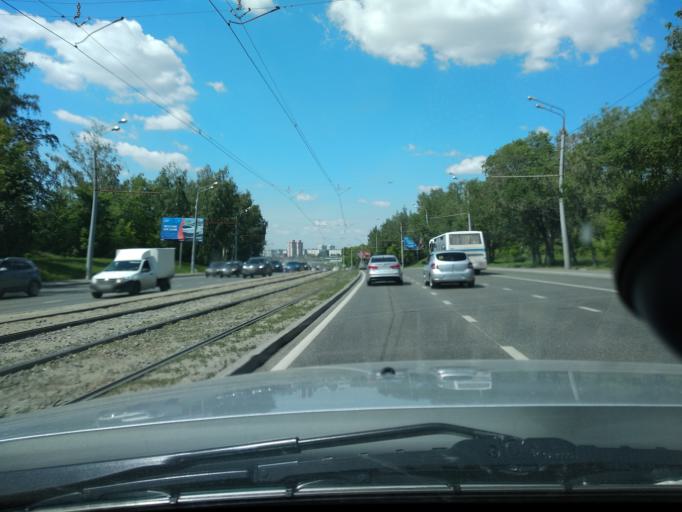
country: RU
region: Tatarstan
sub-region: Gorod Kazan'
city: Kazan
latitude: 55.8200
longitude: 49.1751
